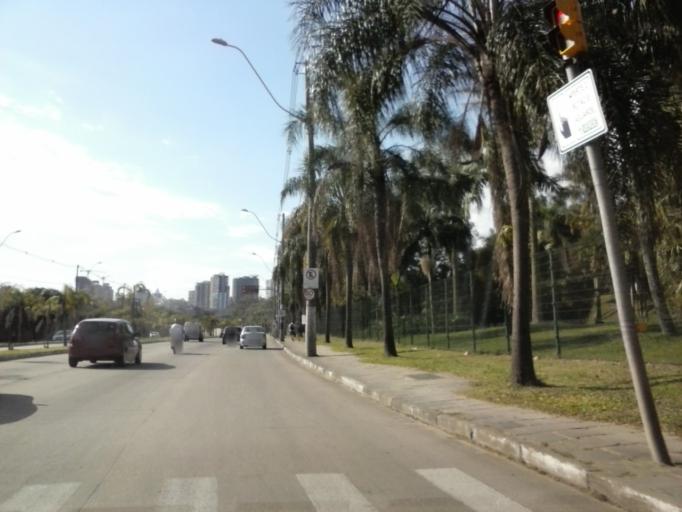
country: BR
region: Rio Grande do Sul
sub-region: Porto Alegre
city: Porto Alegre
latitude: -30.0519
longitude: -51.1809
